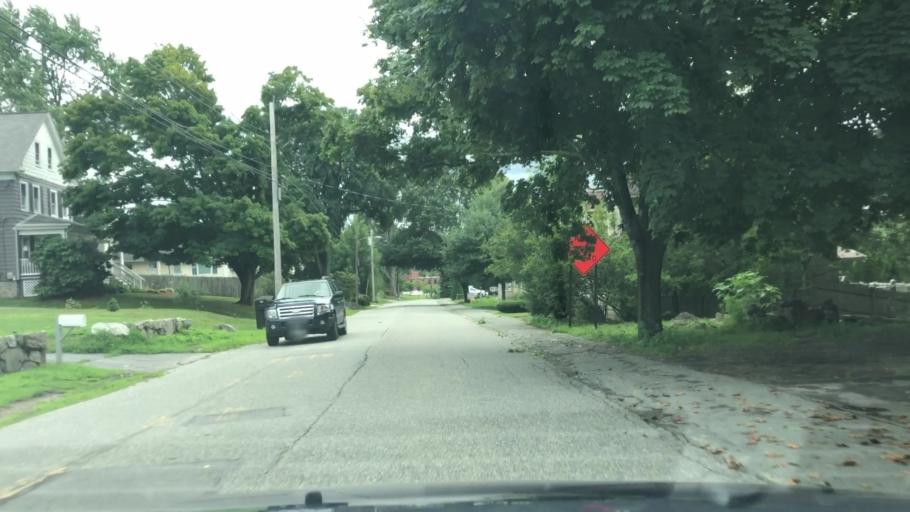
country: US
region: Massachusetts
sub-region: Essex County
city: North Andover
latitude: 42.7053
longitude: -71.1252
